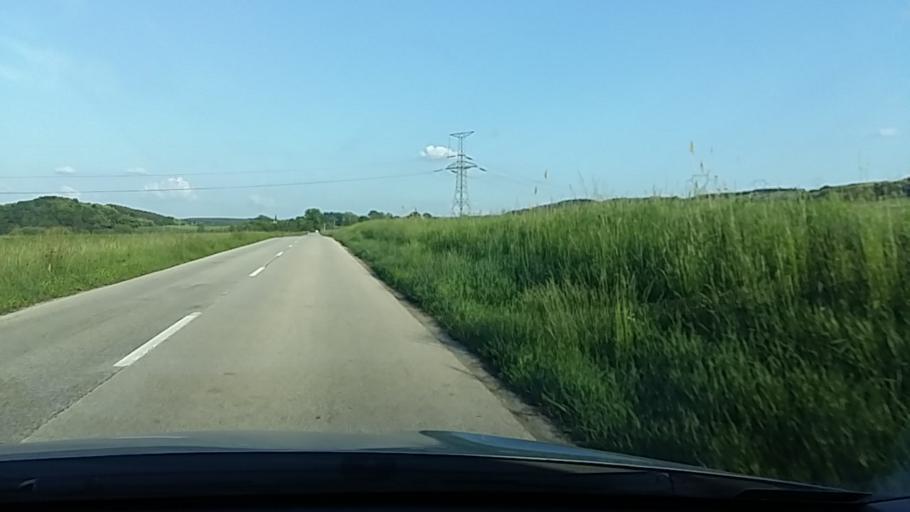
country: HU
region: Pest
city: Szod
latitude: 47.7543
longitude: 19.1982
